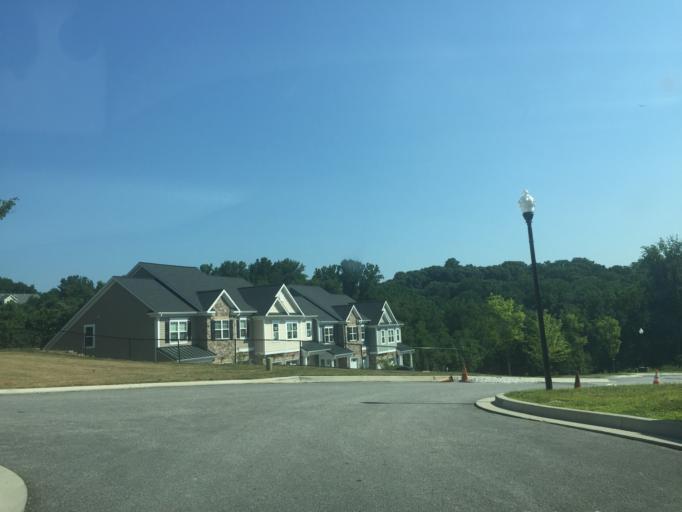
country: US
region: Maryland
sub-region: Baltimore County
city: Mays Chapel
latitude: 39.3898
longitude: -76.6624
